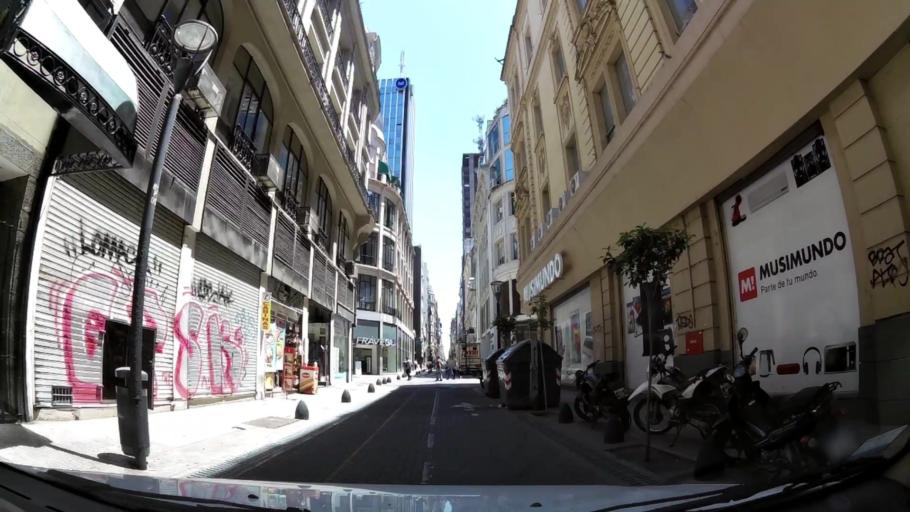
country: AR
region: Buenos Aires F.D.
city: Buenos Aires
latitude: -34.6044
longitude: -58.3746
